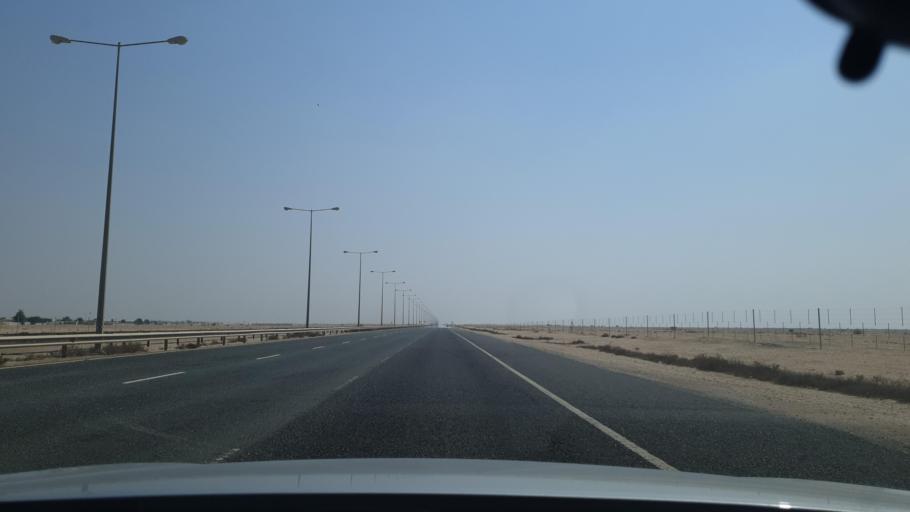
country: QA
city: Al Ghuwayriyah
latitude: 25.8137
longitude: 51.3716
